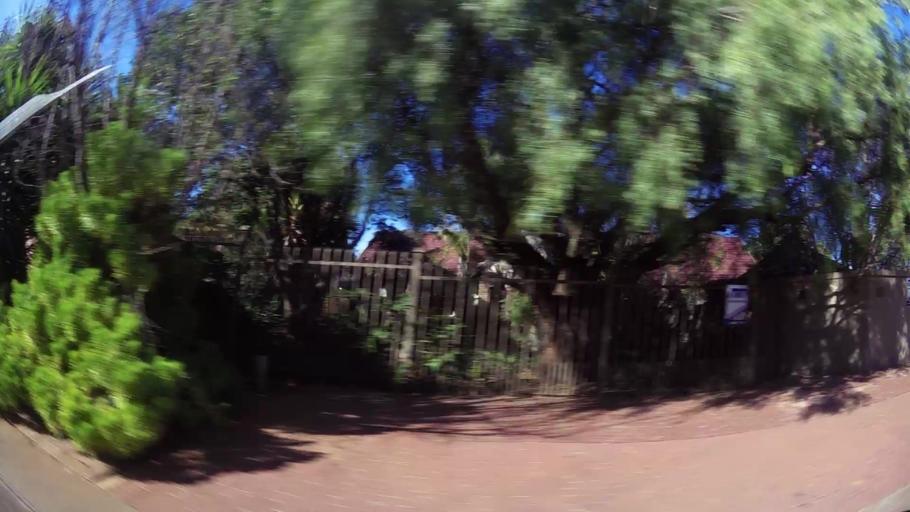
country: ZA
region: Gauteng
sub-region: City of Tshwane Metropolitan Municipality
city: Centurion
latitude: -25.8596
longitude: 28.2114
